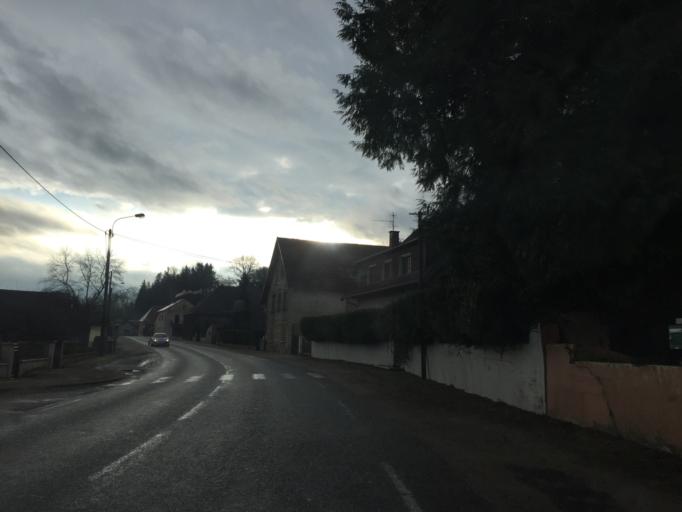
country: FR
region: Franche-Comte
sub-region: Departement du Jura
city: Mont-sous-Vaudrey
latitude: 46.9920
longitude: 5.5576
